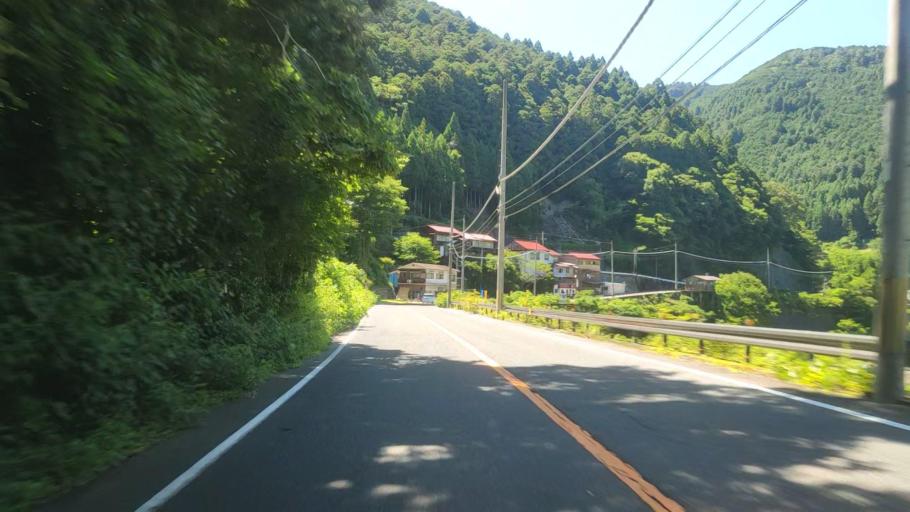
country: JP
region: Nara
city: Yoshino-cho
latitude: 34.2886
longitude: 136.0007
